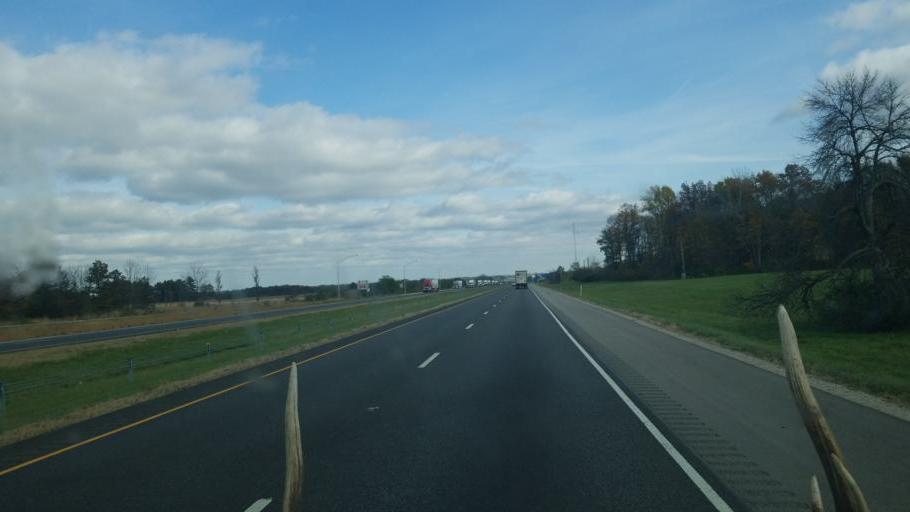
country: US
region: Indiana
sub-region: Wayne County
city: Centerville
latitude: 39.8593
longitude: -85.0236
